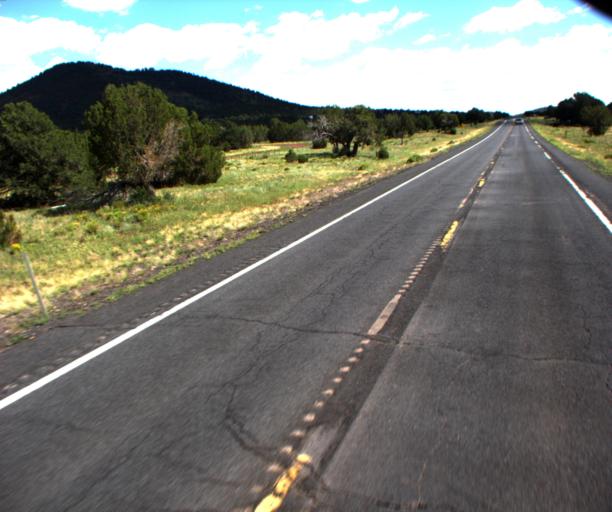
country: US
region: Arizona
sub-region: Coconino County
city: Williams
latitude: 35.3579
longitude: -112.1673
